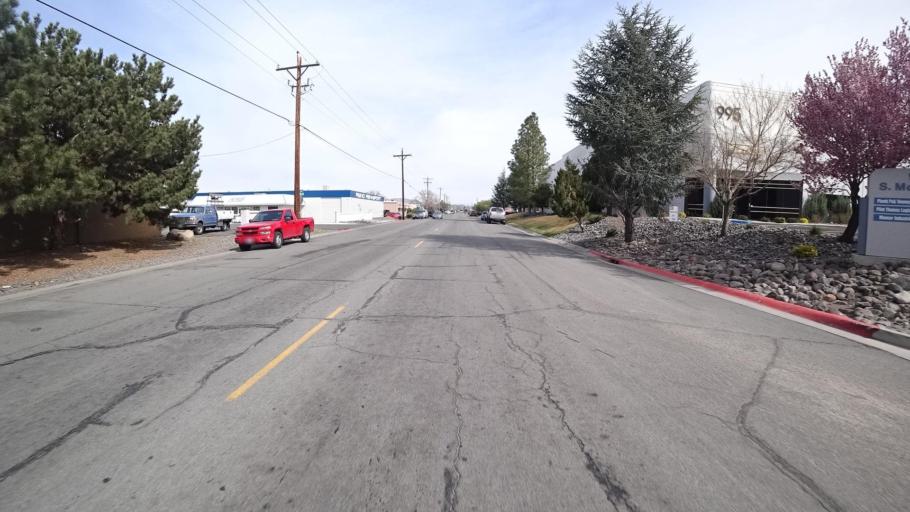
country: US
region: Nevada
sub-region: Washoe County
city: Sparks
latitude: 39.5237
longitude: -119.7434
